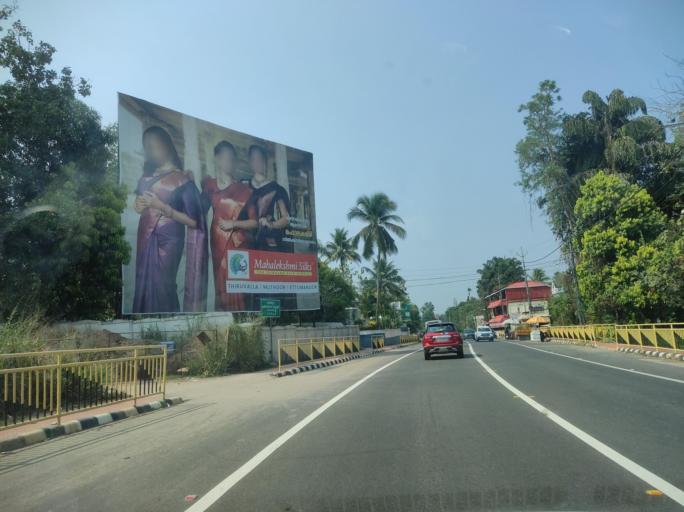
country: IN
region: Kerala
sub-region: Alappuzha
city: Chengannur
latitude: 9.3078
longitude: 76.6225
